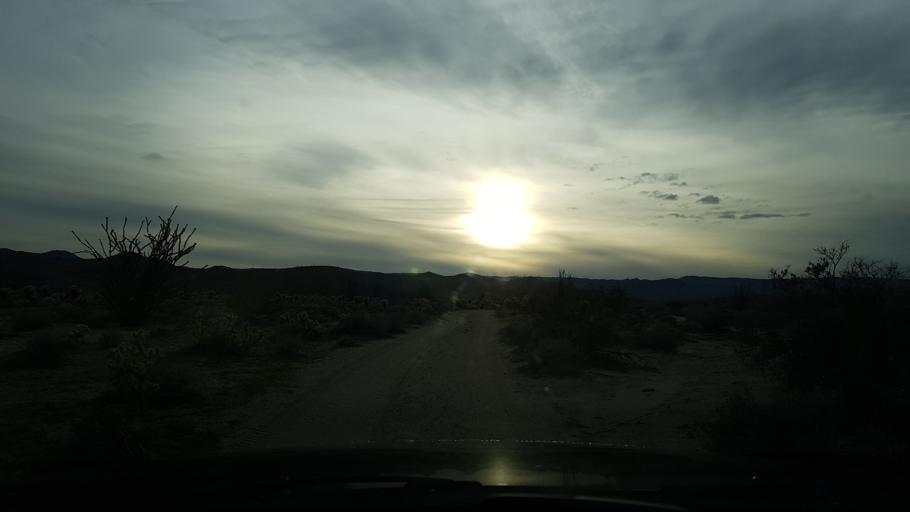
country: MX
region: Baja California
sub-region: Tecate
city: Cereso del Hongo
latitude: 32.8157
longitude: -116.1304
